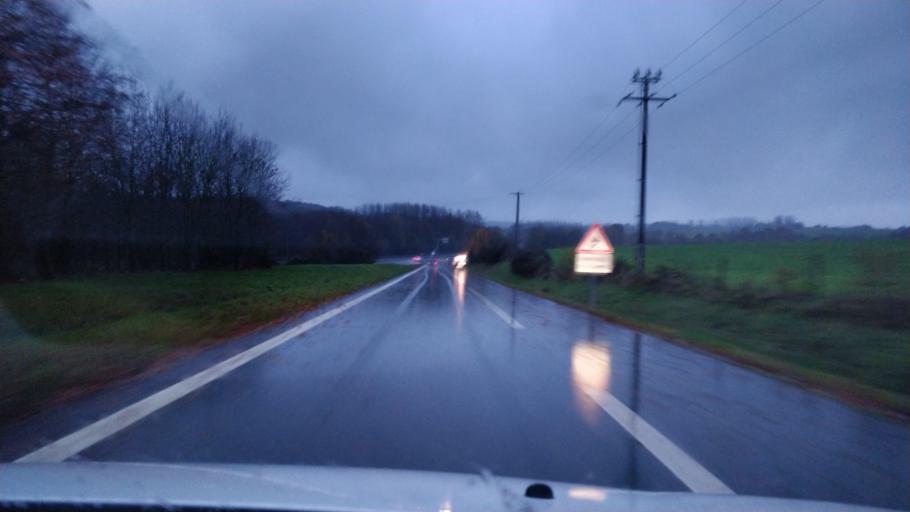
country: FR
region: Brittany
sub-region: Departement du Morbihan
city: Meneac
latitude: 48.1917
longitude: -2.5160
